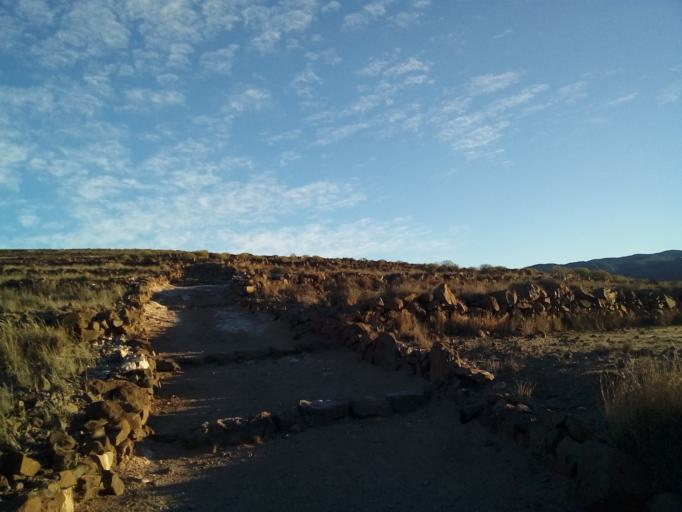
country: ES
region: Canary Islands
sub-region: Provincia de Santa Cruz de Tenerife
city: Vallehermosa
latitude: 28.1067
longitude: -17.3368
